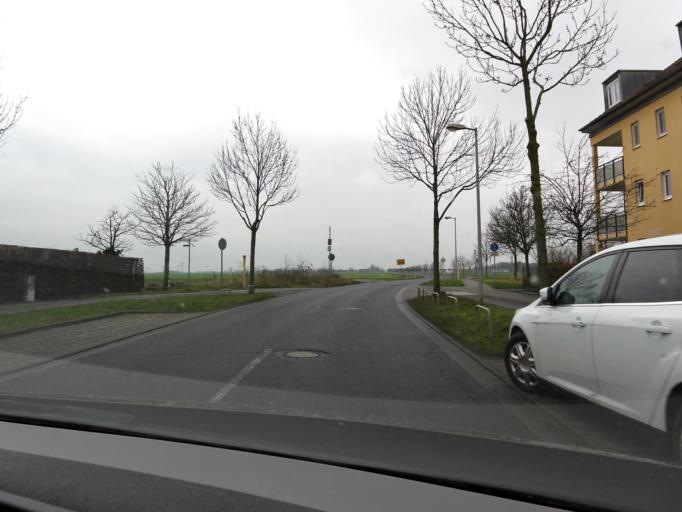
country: DE
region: Saxony
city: Markranstadt
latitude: 51.2995
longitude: 12.2612
